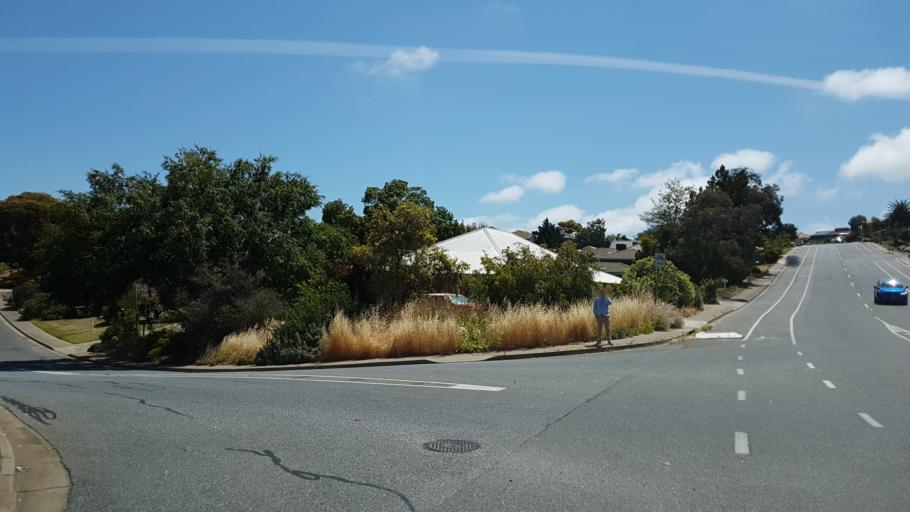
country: AU
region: South Australia
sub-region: Marion
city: Marino
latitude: -35.0656
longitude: 138.5088
